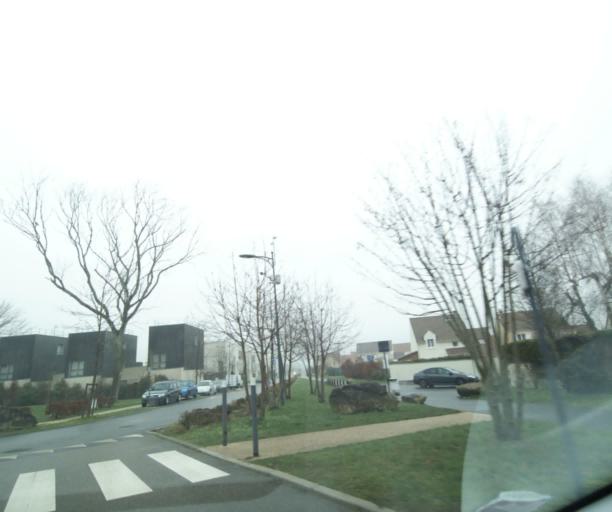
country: FR
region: Ile-de-France
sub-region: Departement de Seine-et-Marne
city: Dammartin-en-Goele
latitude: 49.0608
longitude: 2.6770
